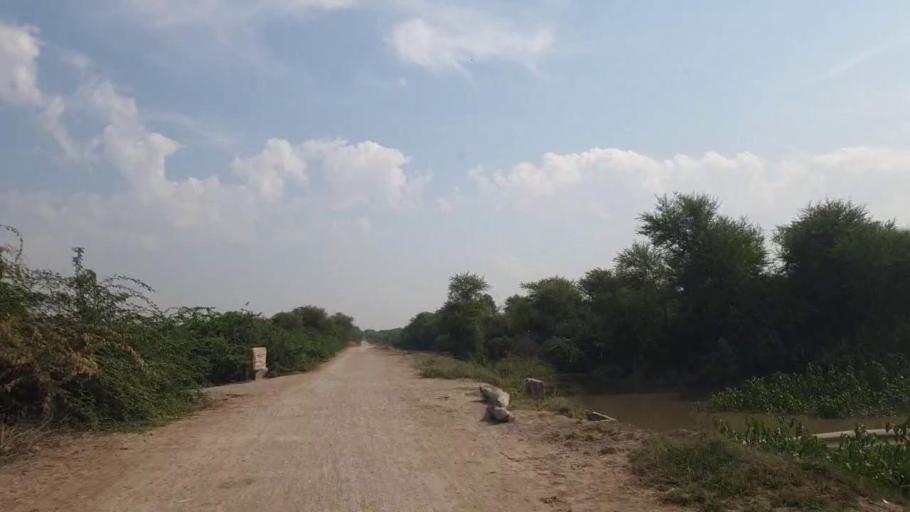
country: PK
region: Sindh
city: Tando Bago
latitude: 24.9274
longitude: 69.0131
